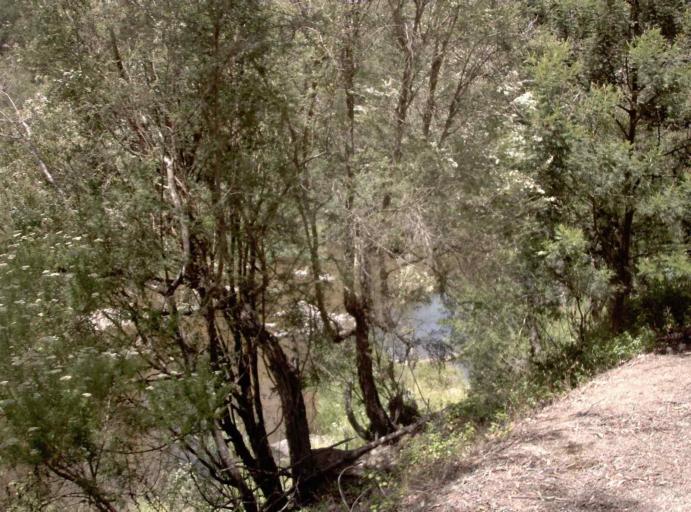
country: AU
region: Victoria
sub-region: East Gippsland
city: Bairnsdale
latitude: -37.4558
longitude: 147.8259
